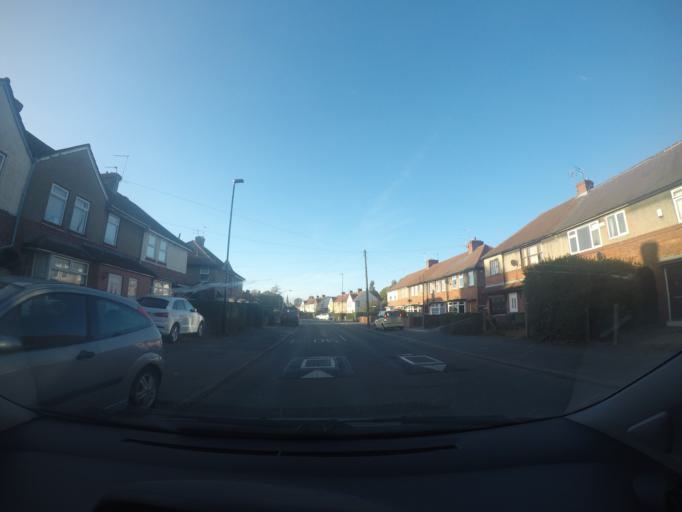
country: GB
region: England
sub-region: City of York
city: Heslington
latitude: 53.9624
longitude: -1.0535
